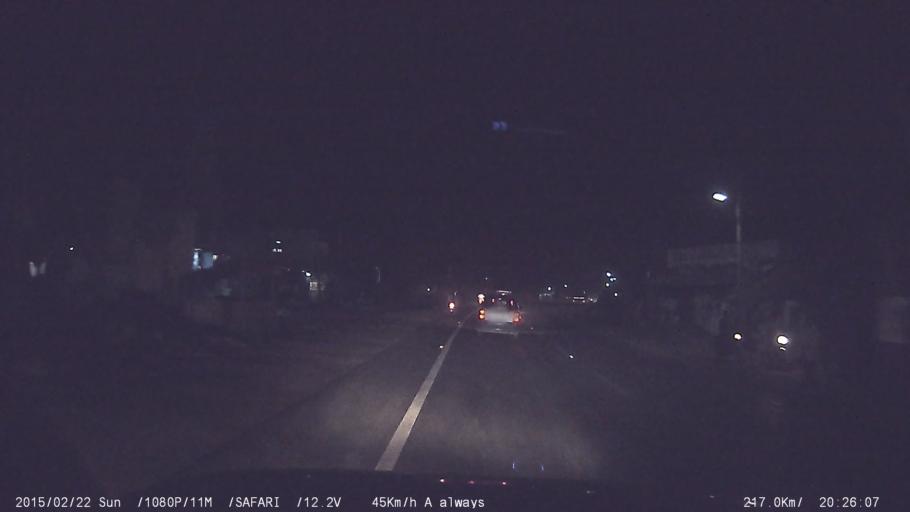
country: IN
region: Tamil Nadu
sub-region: Dindigul
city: Dindigul
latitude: 10.3202
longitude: 77.9071
